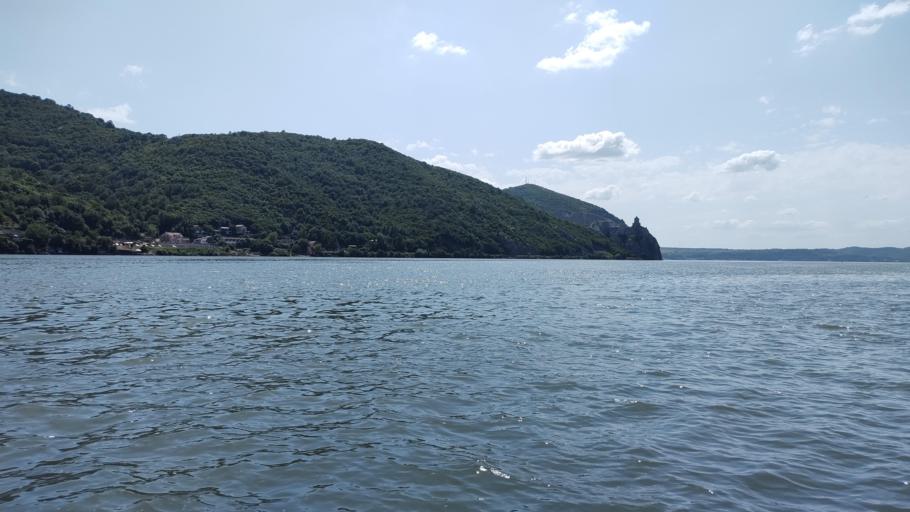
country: RO
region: Caras-Severin
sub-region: Comuna Pescari
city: Coronini
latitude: 44.6643
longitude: 21.6929
